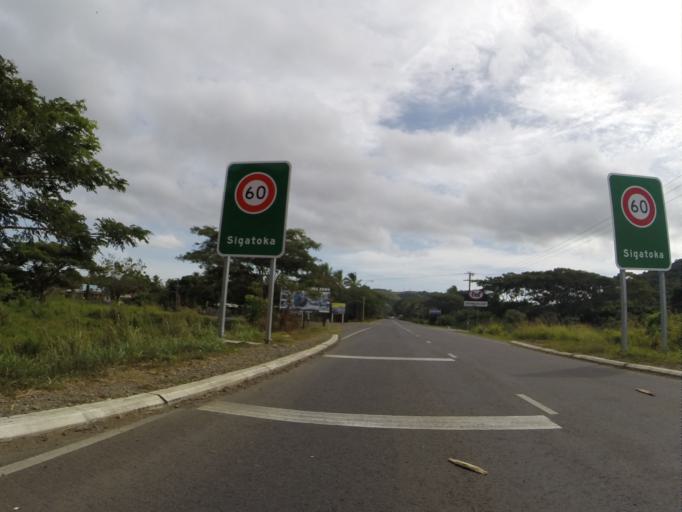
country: FJ
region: Western
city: Nadi
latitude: -18.1459
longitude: 177.5127
